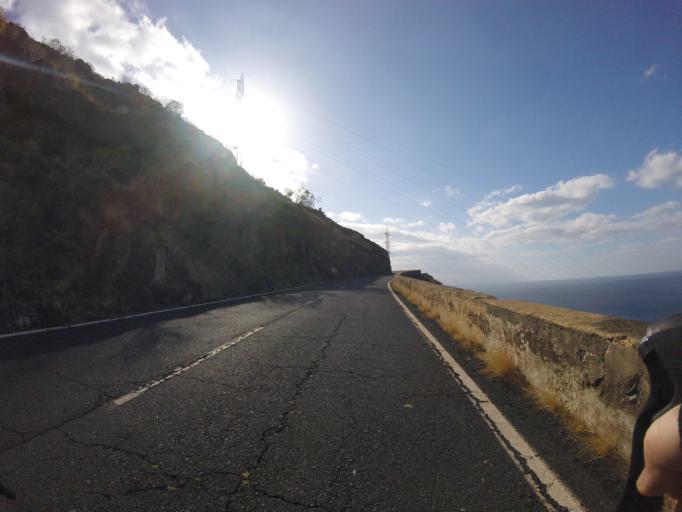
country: ES
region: Canary Islands
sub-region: Provincia de Santa Cruz de Tenerife
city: Candelaria
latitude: 28.3855
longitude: -16.3578
